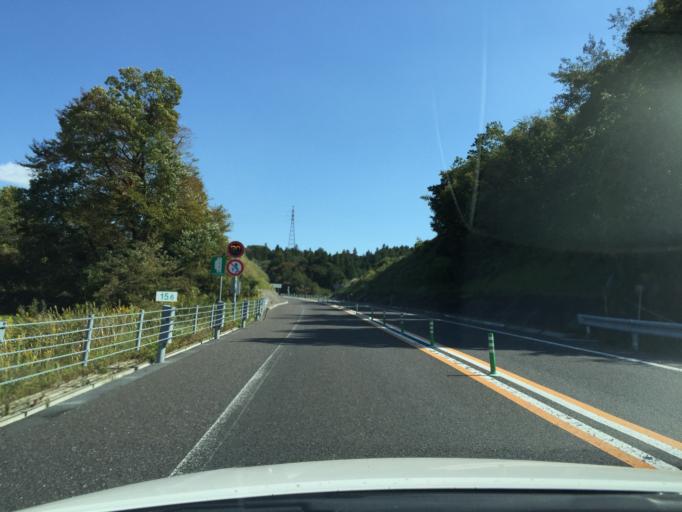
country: JP
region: Fukushima
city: Ishikawa
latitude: 37.1999
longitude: 140.4612
